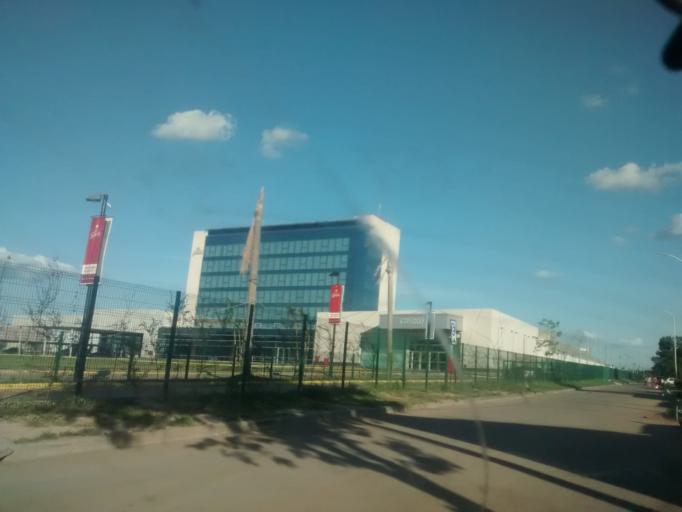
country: AR
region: Chaco
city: Fontana
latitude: -27.4470
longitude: -59.0236
